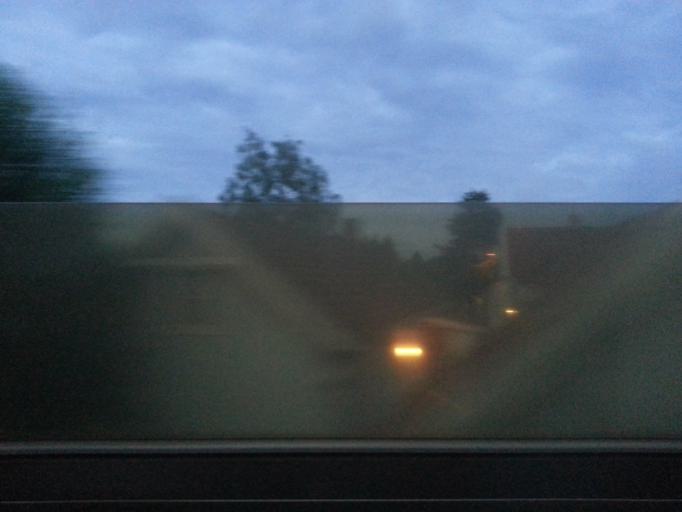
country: NO
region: Akershus
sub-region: Skedsmo
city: Lillestrom
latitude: 59.9566
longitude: 11.0570
